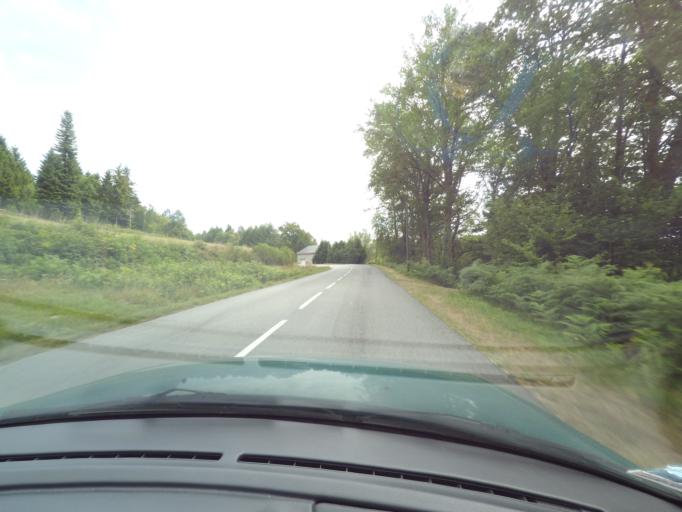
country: FR
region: Limousin
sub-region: Departement de la Haute-Vienne
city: Eymoutiers
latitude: 45.7220
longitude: 1.8718
